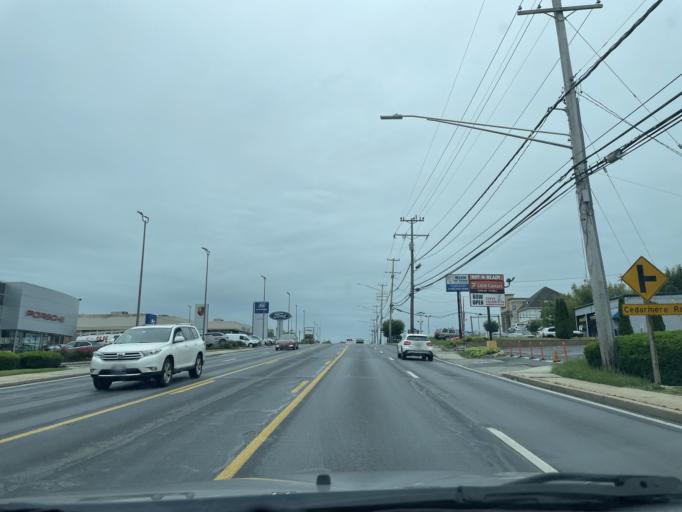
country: US
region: Maryland
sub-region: Baltimore County
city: Owings Mills
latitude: 39.4371
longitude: -76.8018
